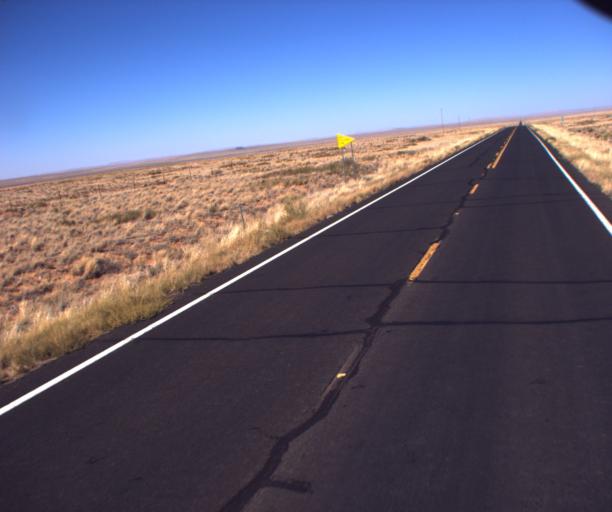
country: US
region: Arizona
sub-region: Navajo County
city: Dilkon
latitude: 35.5147
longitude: -110.4397
